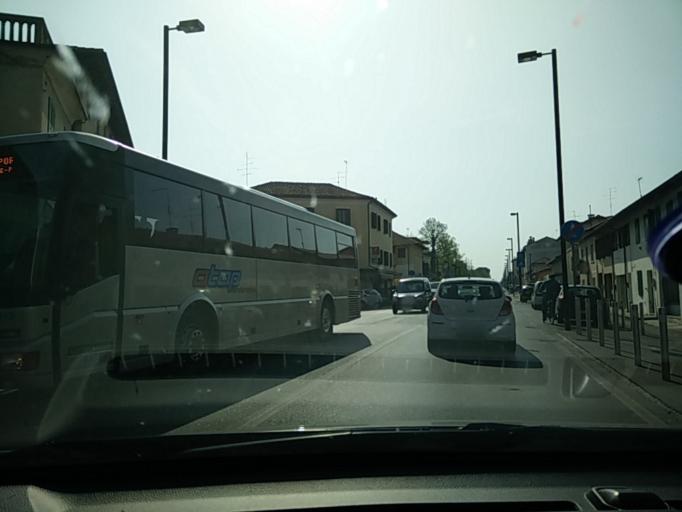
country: IT
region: Friuli Venezia Giulia
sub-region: Provincia di Pordenone
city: Pordenone
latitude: 45.9525
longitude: 12.6706
